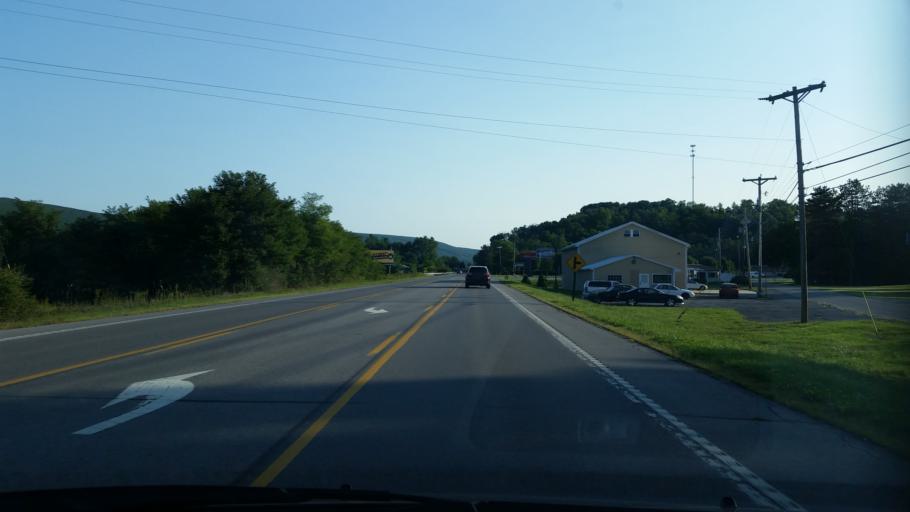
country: US
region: Pennsylvania
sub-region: Blair County
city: Bellwood
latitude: 40.5954
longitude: -78.3219
